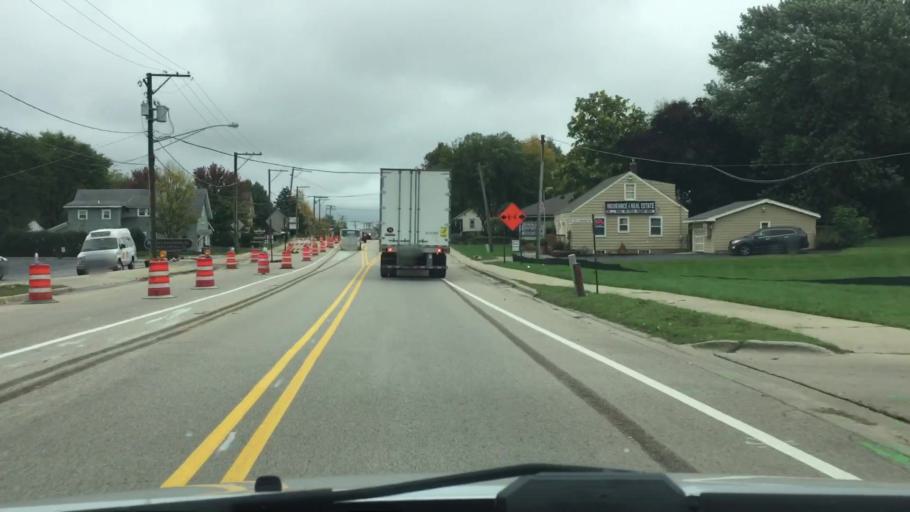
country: US
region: Illinois
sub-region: Kane County
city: Sleepy Hollow
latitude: 42.1099
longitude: -88.2958
